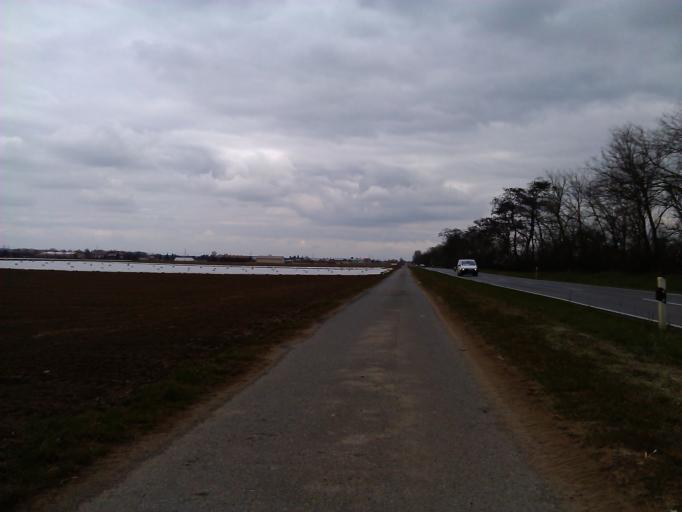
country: DE
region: Hesse
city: Griesheim
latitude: 49.8394
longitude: 8.5611
